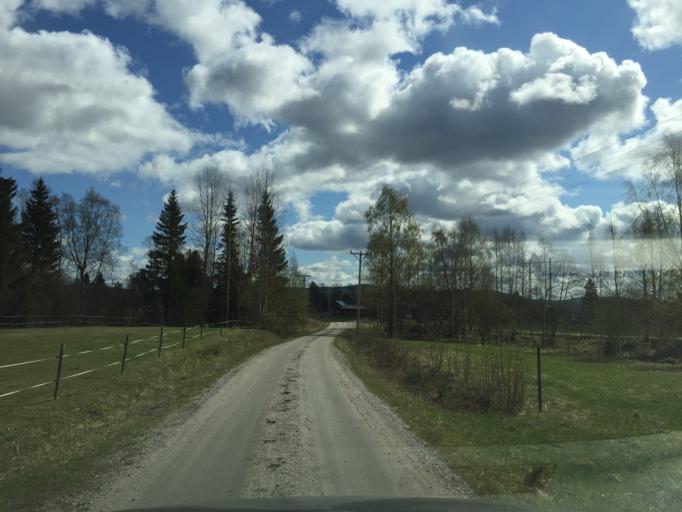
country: SE
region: Gaevleborg
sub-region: Bollnas Kommun
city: Arbra
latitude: 61.5209
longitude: 16.3379
